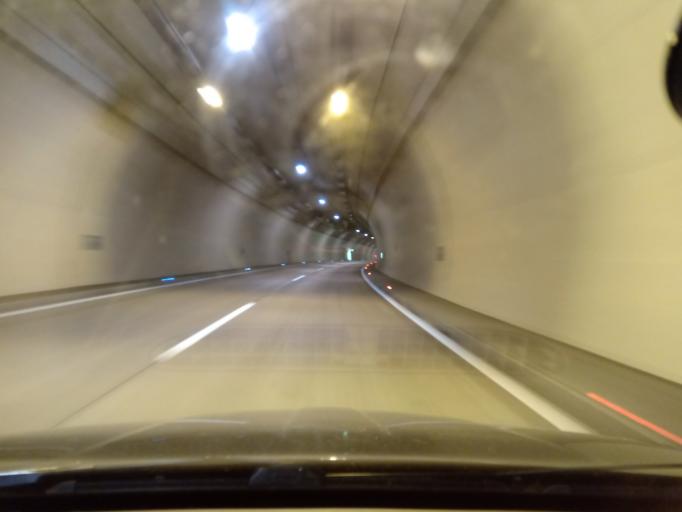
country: AT
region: Styria
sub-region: Politischer Bezirk Bruck-Muerzzuschlag
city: Pernegg an der Mur
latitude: 47.3698
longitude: 15.3145
